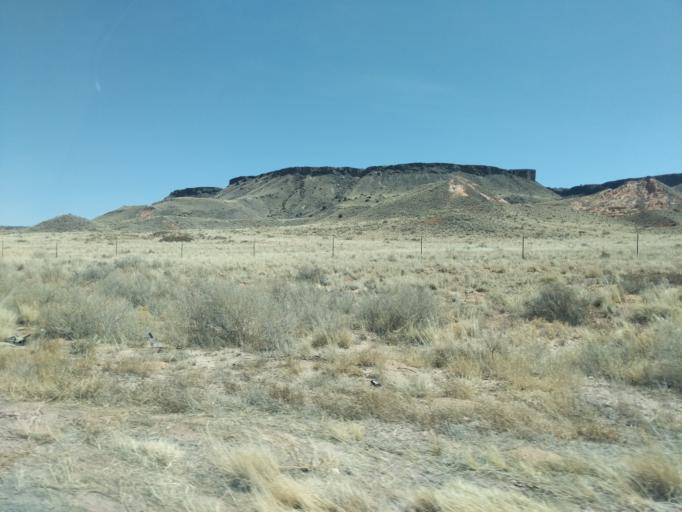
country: US
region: Arizona
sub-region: Navajo County
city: Dilkon
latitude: 35.4360
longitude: -110.0658
